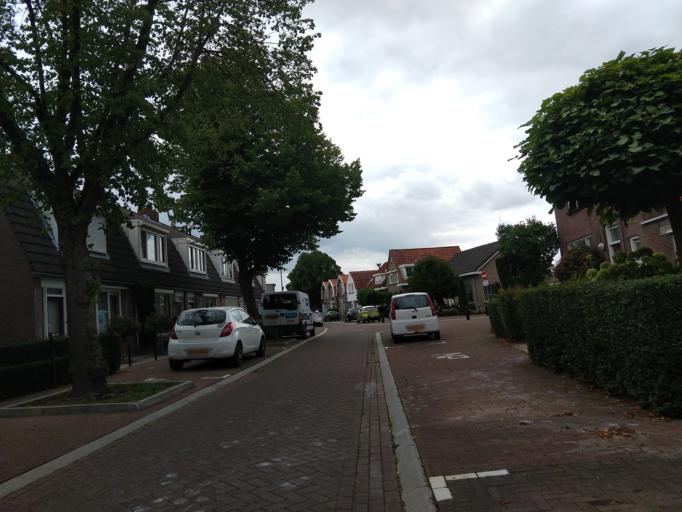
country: NL
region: Zeeland
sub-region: Gemeente Vlissingen
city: Vlissingen
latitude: 51.4624
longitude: 3.5983
